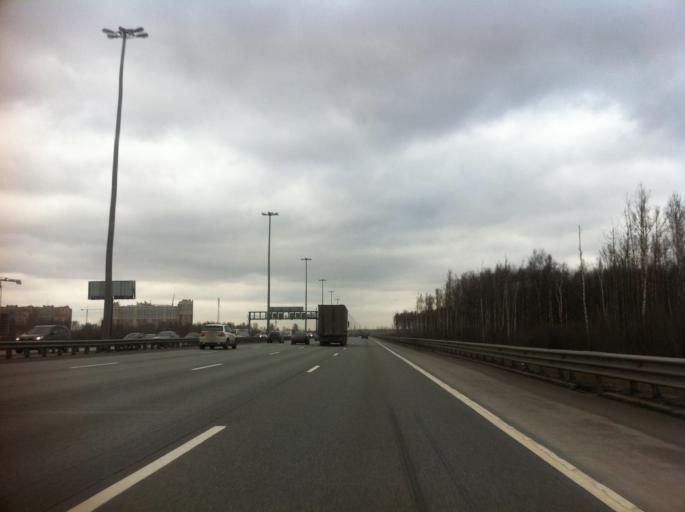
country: RU
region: Leningrad
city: Rybatskoye
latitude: 59.9040
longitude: 30.5266
